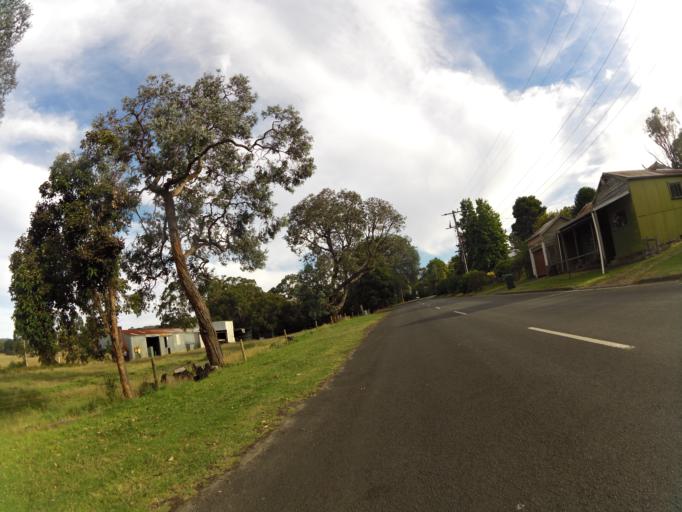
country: AU
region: Victoria
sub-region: Colac-Otway
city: Colac
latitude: -38.5182
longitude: 143.7168
